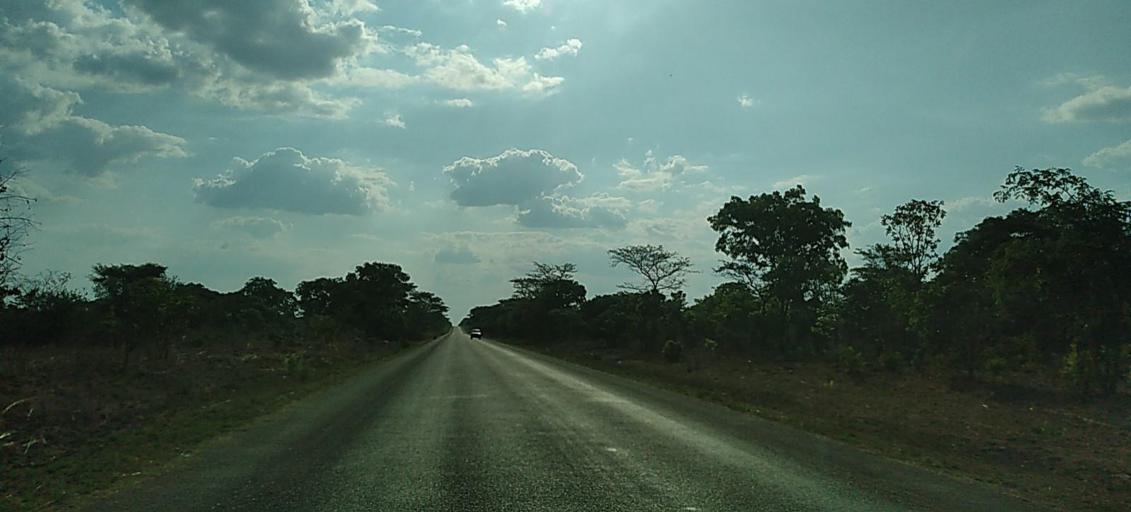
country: ZM
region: Copperbelt
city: Luanshya
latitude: -13.3881
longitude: 28.3844
